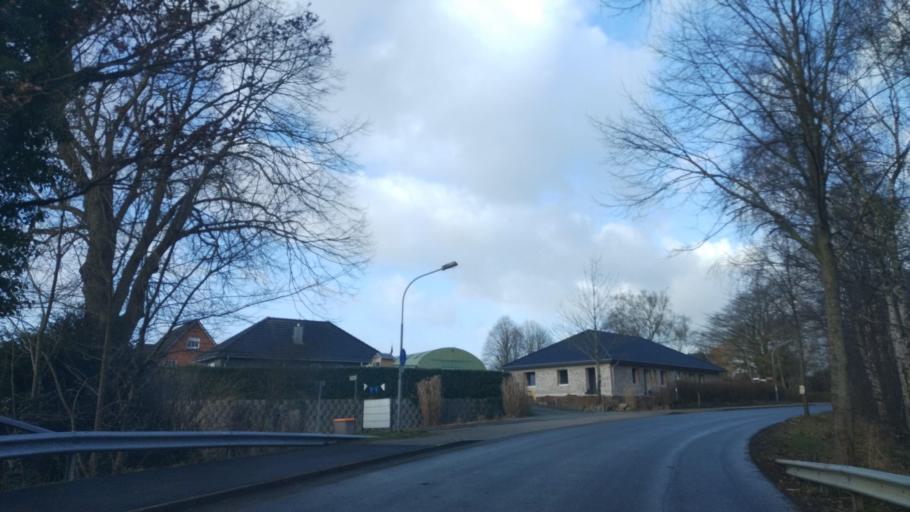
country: DE
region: Schleswig-Holstein
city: Taarstedt
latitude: 54.5635
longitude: 9.6790
